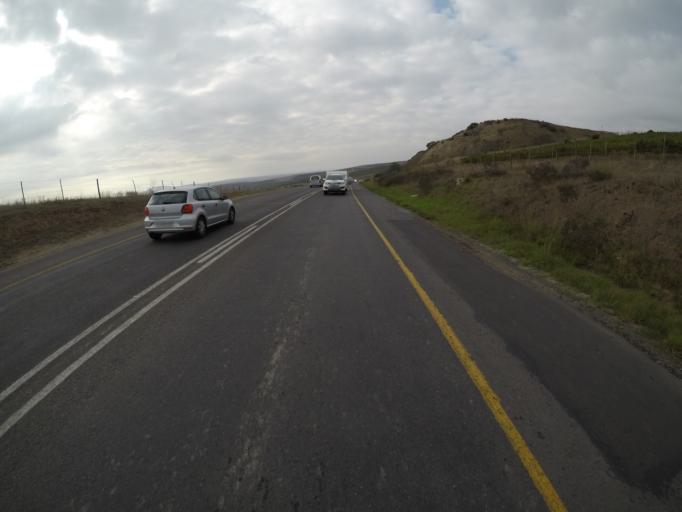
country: ZA
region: Western Cape
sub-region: City of Cape Town
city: Sunset Beach
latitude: -33.8329
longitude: 18.5900
